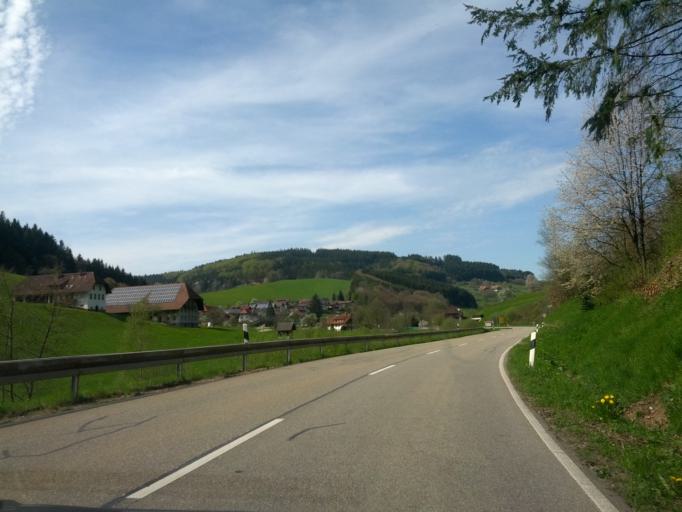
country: DE
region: Baden-Wuerttemberg
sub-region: Freiburg Region
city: Elzach
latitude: 48.1885
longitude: 8.0473
